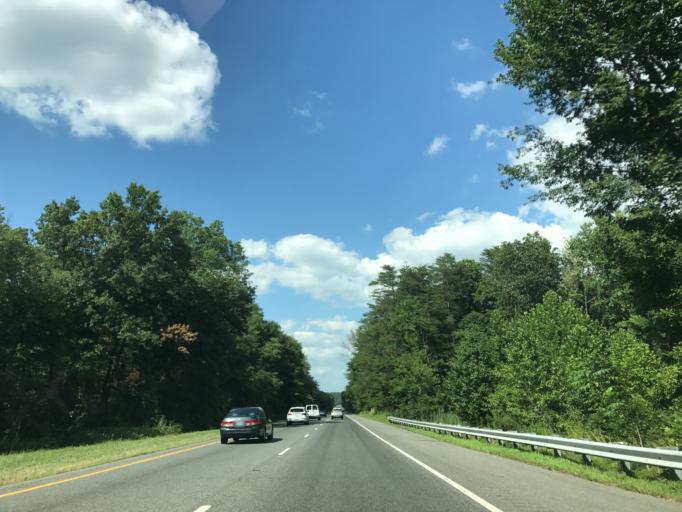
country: US
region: Maryland
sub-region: Howard County
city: Hanover
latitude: 39.1774
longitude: -76.7241
